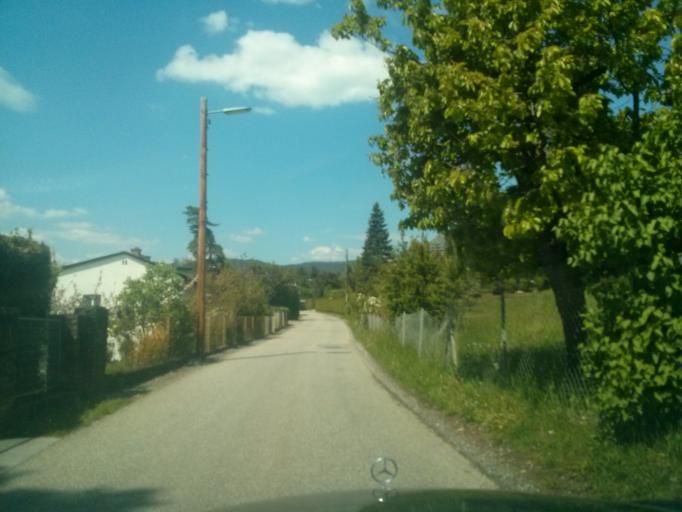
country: AT
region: Styria
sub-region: Politischer Bezirk Graz-Umgebung
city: Stattegg
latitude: 47.1210
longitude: 15.4181
